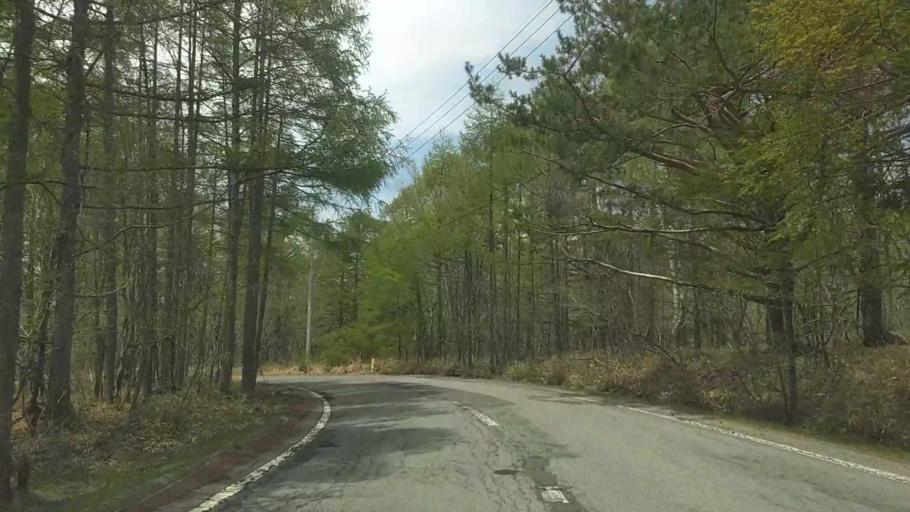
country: JP
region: Nagano
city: Chino
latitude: 36.0497
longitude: 138.3087
